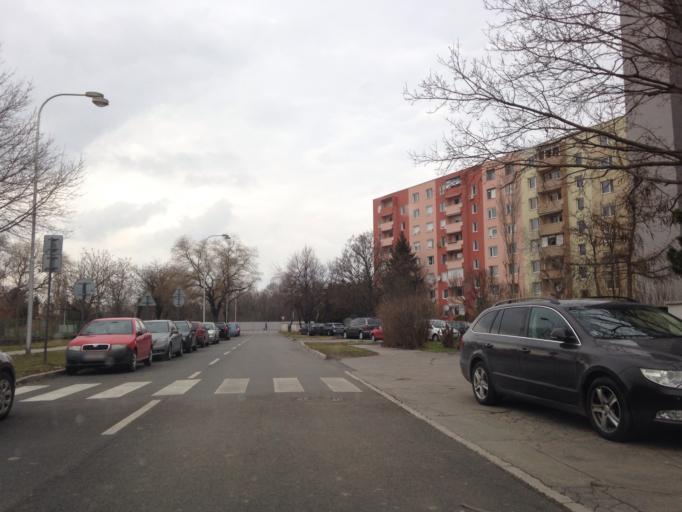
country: SK
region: Nitriansky
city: Komarno
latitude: 47.7630
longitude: 18.1203
